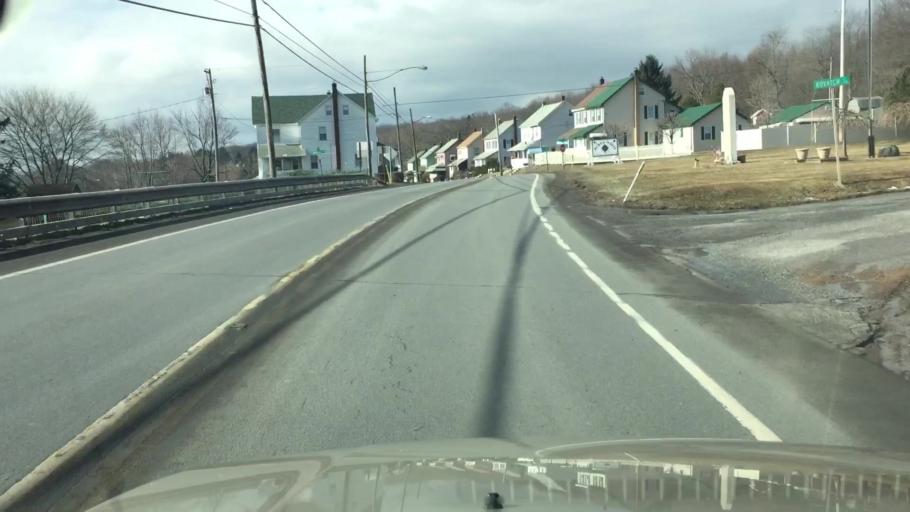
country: US
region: Pennsylvania
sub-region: Luzerne County
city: Oakdale
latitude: 40.9921
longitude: -75.9111
